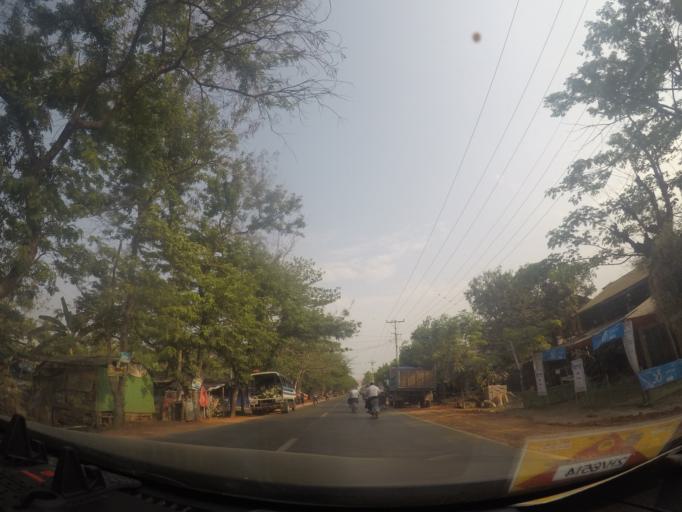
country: MM
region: Bago
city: Paungde
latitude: 18.3395
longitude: 95.6225
